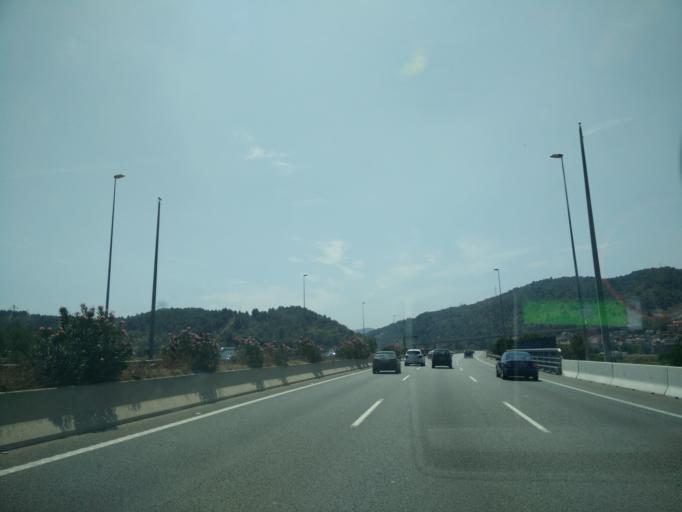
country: ES
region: Catalonia
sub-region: Provincia de Barcelona
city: Martorell
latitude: 41.4827
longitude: 1.9355
